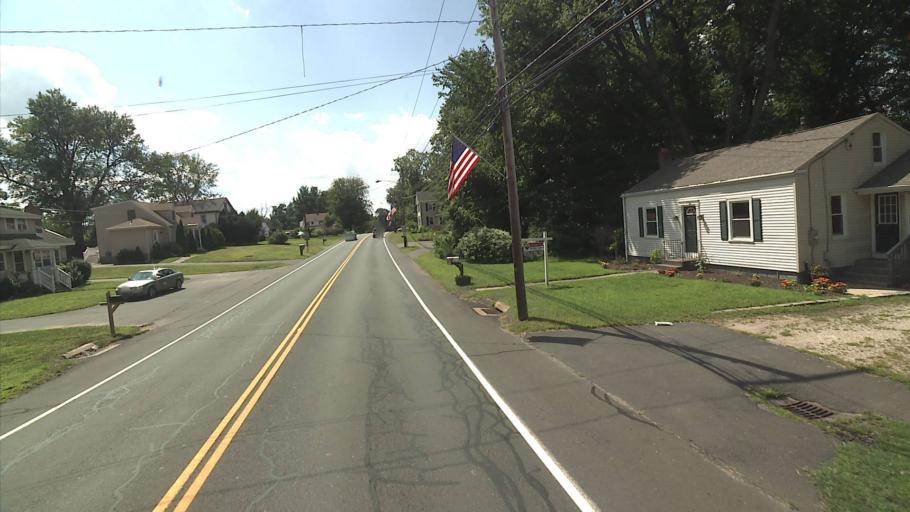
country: US
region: Connecticut
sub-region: Tolland County
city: Somers
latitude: 41.9850
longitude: -72.4500
